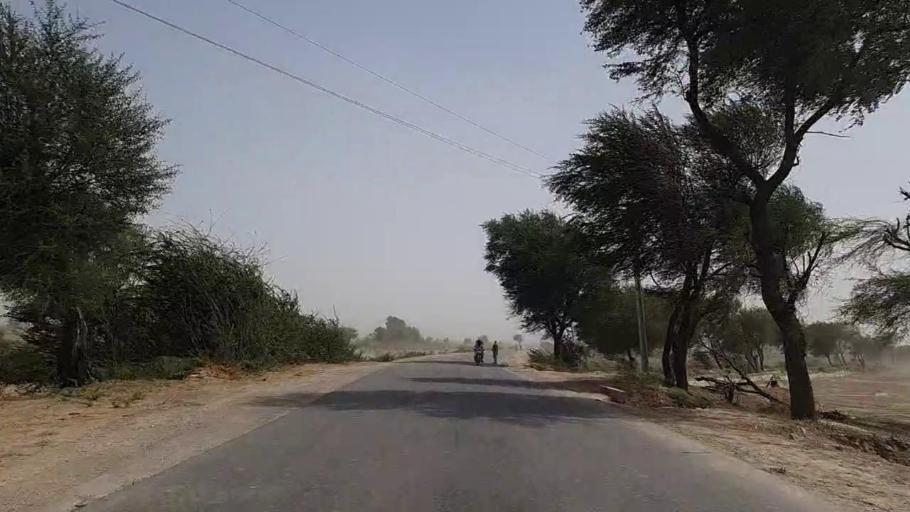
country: PK
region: Sindh
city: Talhar
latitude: 24.8720
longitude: 68.8398
